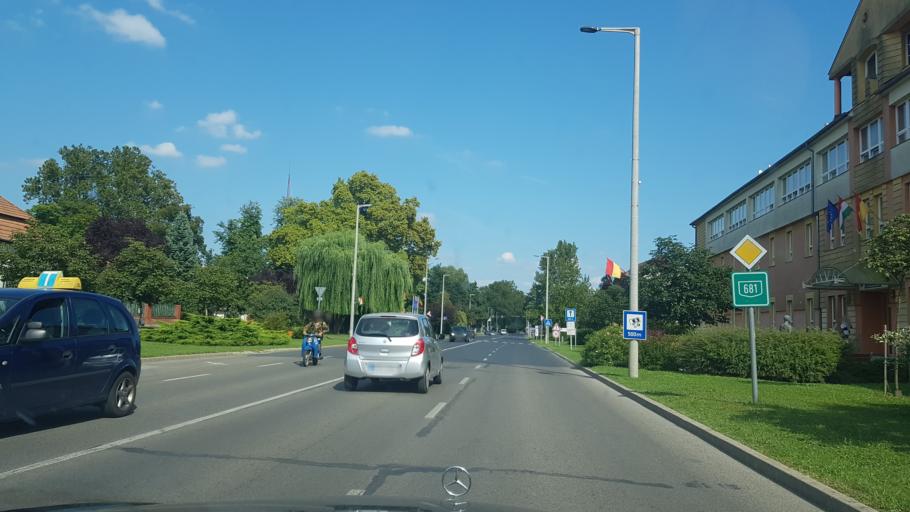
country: HU
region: Somogy
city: Nagyatad
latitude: 46.2298
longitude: 17.3580
